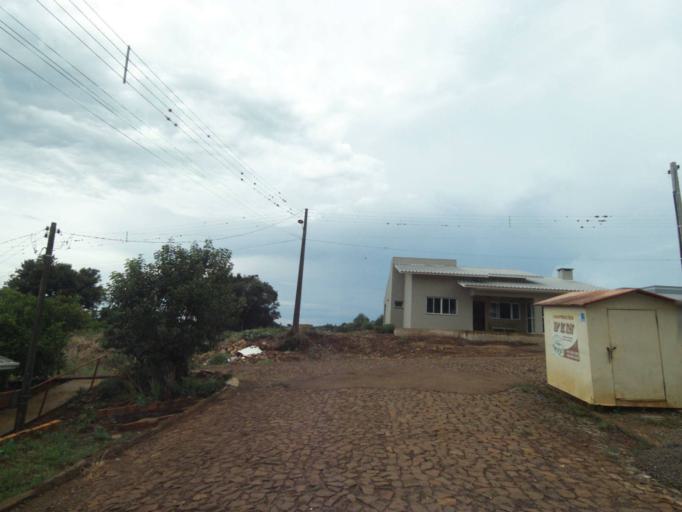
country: BR
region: Parana
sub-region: Guaraniacu
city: Guaraniacu
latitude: -25.0946
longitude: -52.8682
